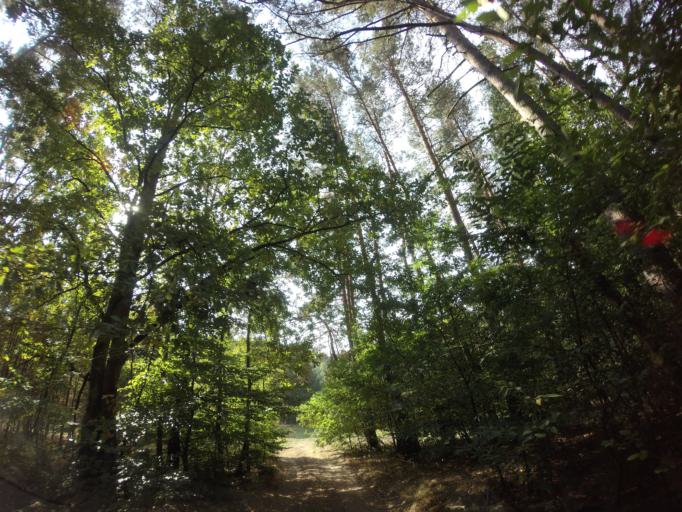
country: PL
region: West Pomeranian Voivodeship
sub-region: Powiat drawski
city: Drawsko Pomorskie
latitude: 53.4578
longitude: 15.7289
